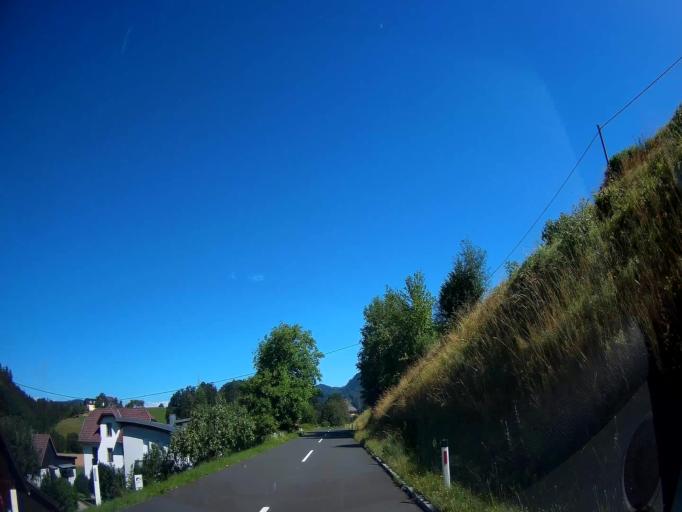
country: AT
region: Carinthia
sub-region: Politischer Bezirk Volkermarkt
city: Voelkermarkt
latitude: 46.6807
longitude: 14.5769
